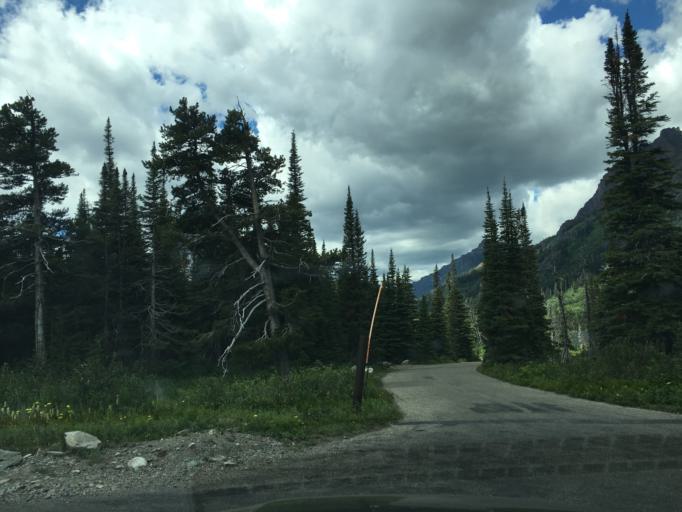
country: US
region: Montana
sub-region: Glacier County
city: South Browning
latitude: 48.4862
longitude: -113.3672
